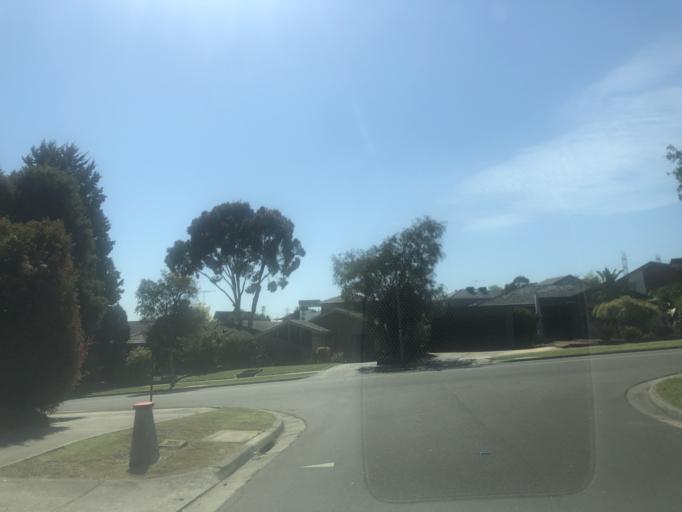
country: AU
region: Victoria
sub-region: Monash
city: Mulgrave
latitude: -37.9001
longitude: 145.1768
